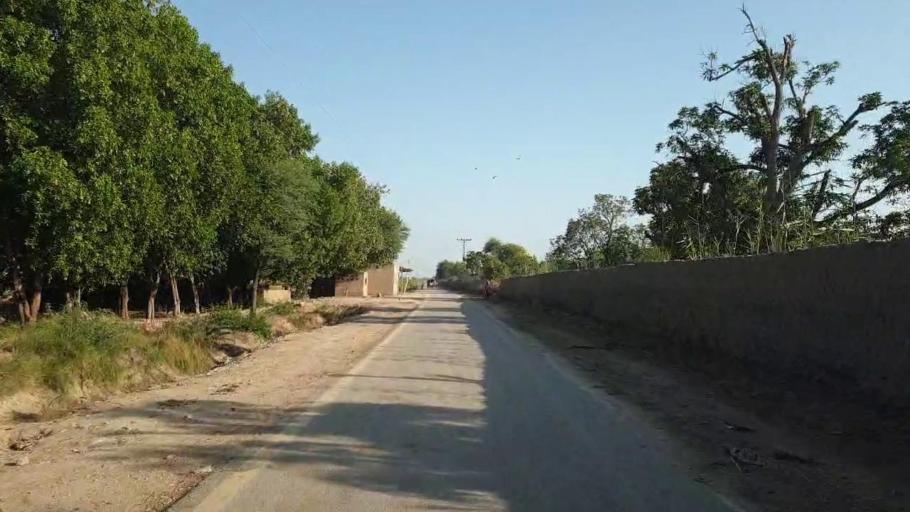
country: PK
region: Sindh
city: Hyderabad
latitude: 25.3404
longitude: 68.4196
